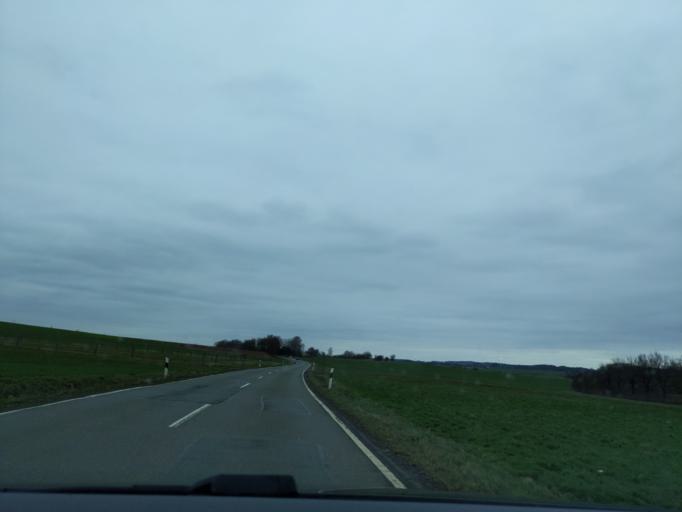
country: DE
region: Hesse
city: Frankenberg
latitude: 51.0390
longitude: 8.8194
